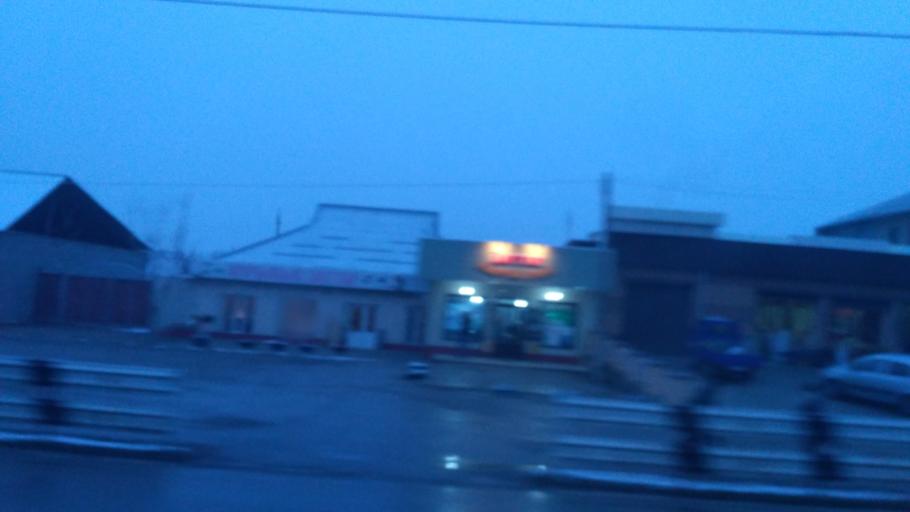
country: KZ
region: Ongtustik Qazaqstan
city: Shymkent
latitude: 42.3657
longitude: 69.5148
